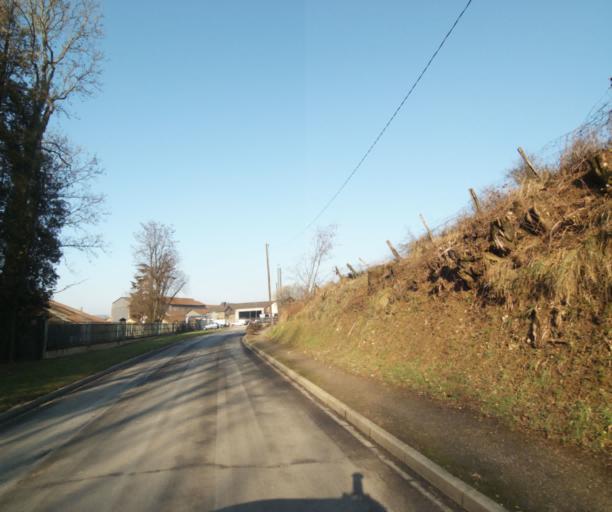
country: FR
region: Champagne-Ardenne
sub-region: Departement de la Haute-Marne
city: Wassy
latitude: 48.4869
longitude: 4.9684
